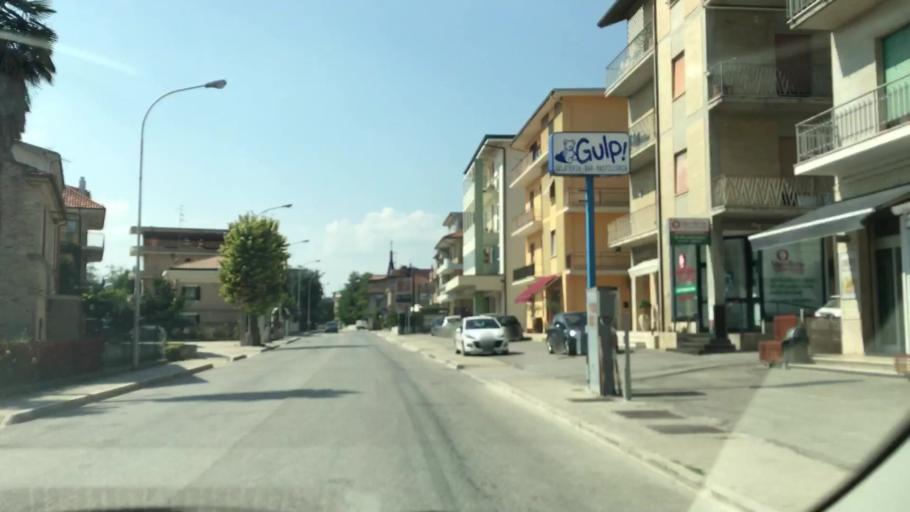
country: IT
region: The Marches
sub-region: Provincia di Ascoli Piceno
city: Stella
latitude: 42.8880
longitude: 13.8135
